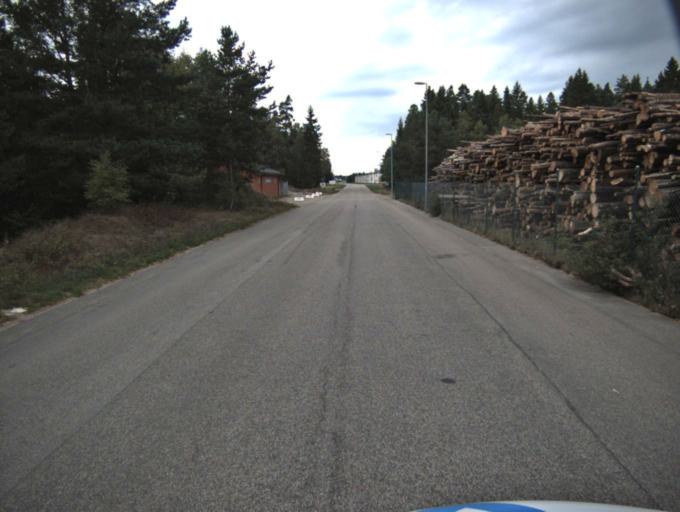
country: SE
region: Vaestra Goetaland
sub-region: Ulricehamns Kommun
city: Ulricehamn
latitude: 57.8295
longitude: 13.4217
